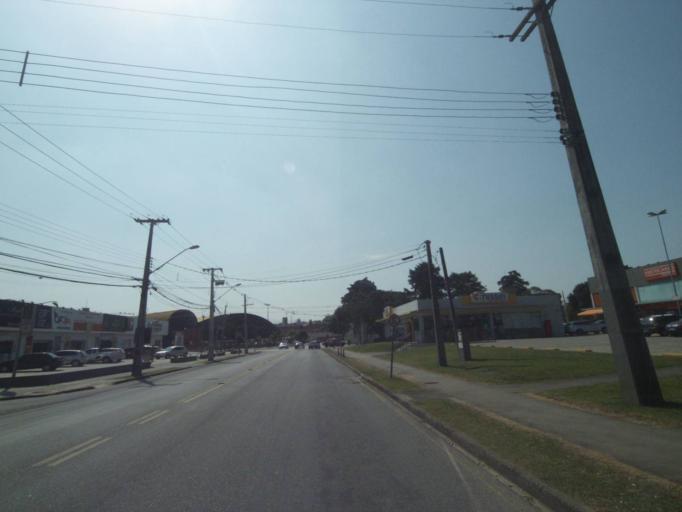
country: BR
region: Parana
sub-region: Curitiba
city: Curitiba
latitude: -25.4788
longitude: -49.3253
